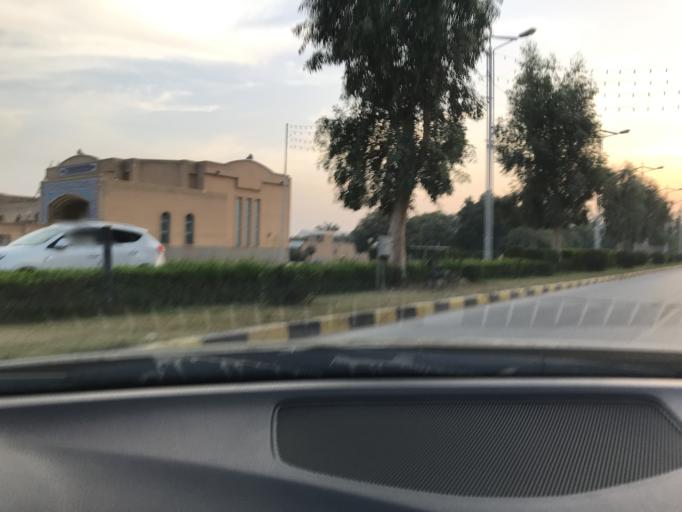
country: IR
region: Khuzestan
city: Ahvaz
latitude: 31.3298
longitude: 48.7362
